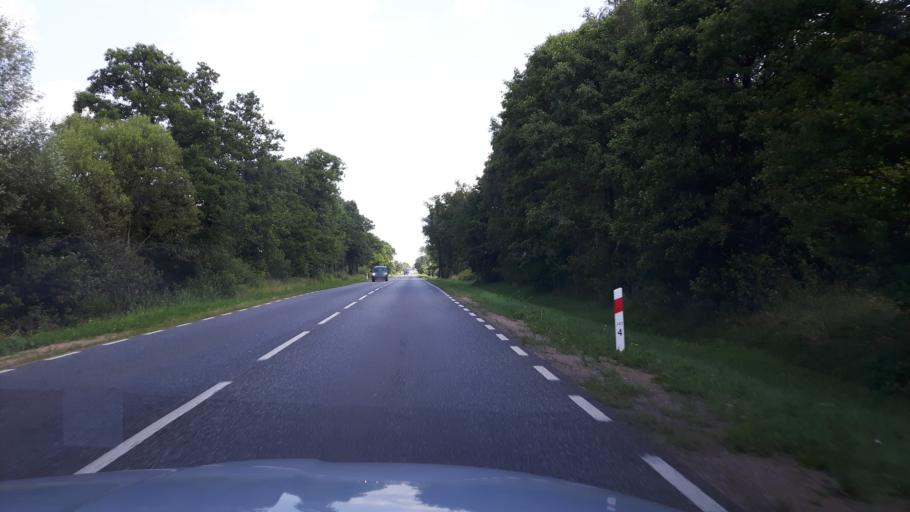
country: PL
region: Masovian Voivodeship
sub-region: Powiat wolominski
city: Jadow
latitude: 52.4655
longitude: 21.6558
